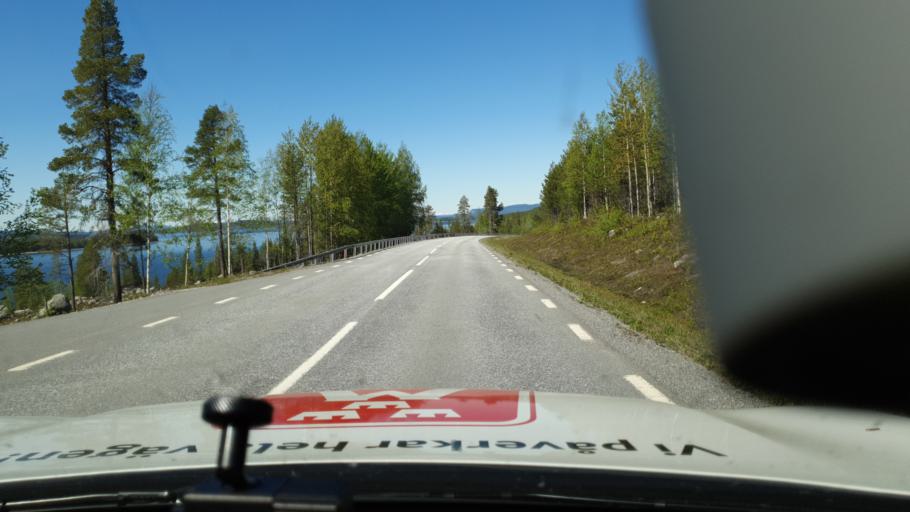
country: SE
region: Vaesterbotten
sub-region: Storumans Kommun
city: Storuman
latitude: 65.1465
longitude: 17.0785
